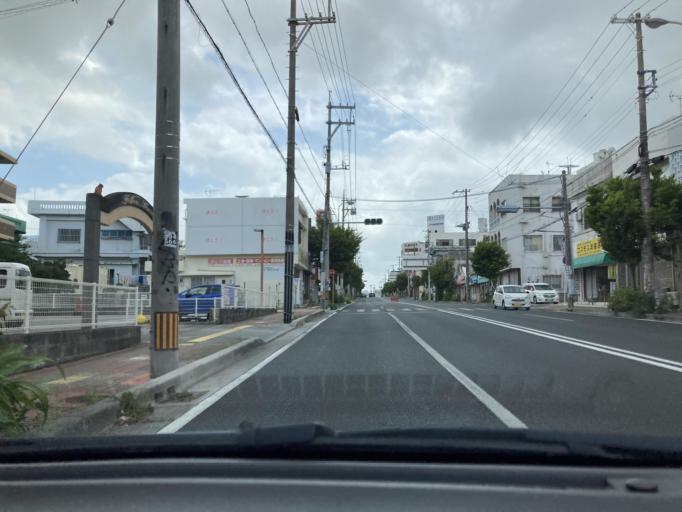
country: JP
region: Okinawa
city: Okinawa
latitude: 26.3384
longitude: 127.8160
